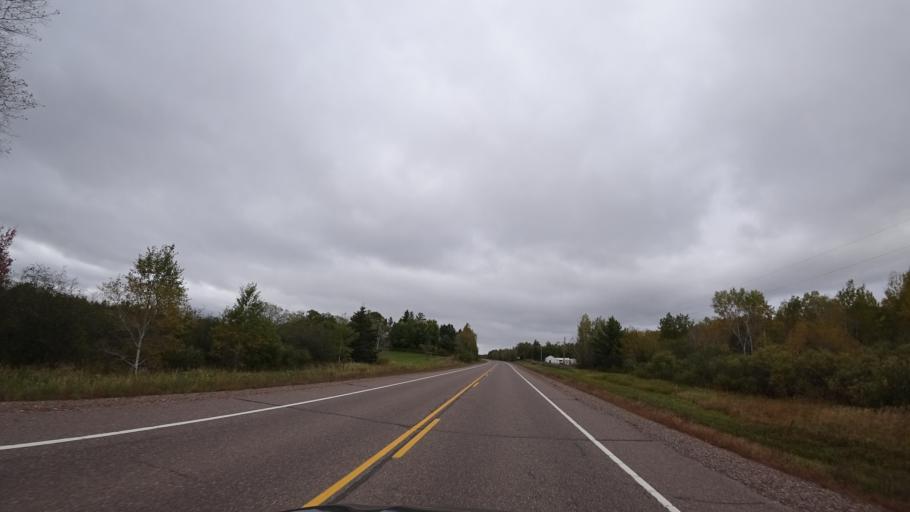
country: US
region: Wisconsin
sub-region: Rusk County
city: Ladysmith
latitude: 45.5532
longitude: -91.1119
